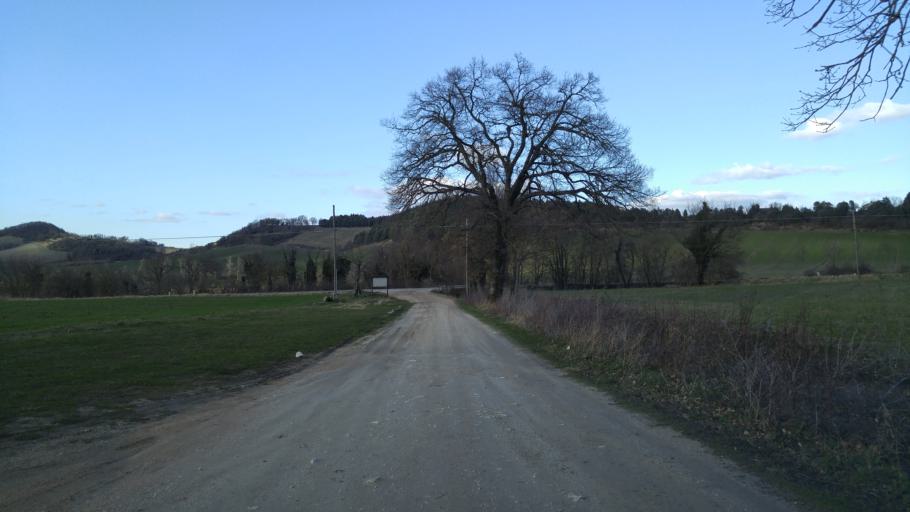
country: IT
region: The Marches
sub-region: Provincia di Pesaro e Urbino
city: Cagli
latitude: 43.5390
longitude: 12.6861
